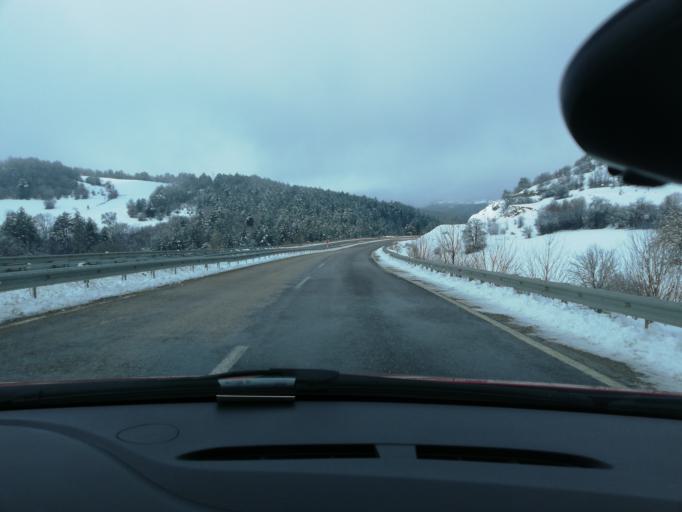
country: TR
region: Kastamonu
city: Akkaya
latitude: 41.2812
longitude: 33.4621
